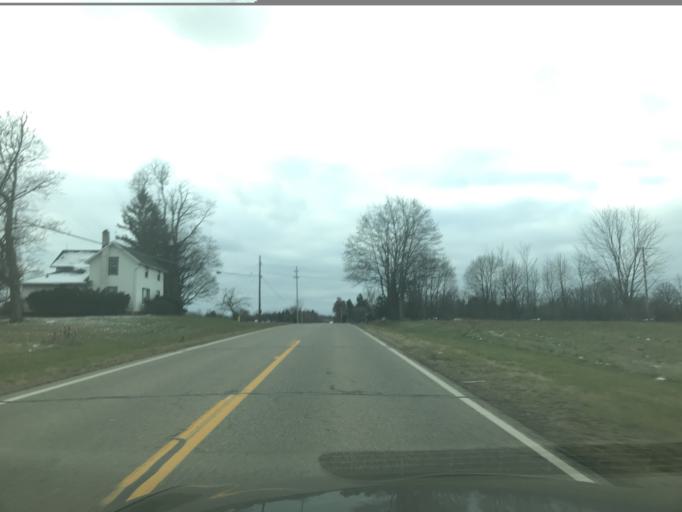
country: US
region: Michigan
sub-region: Eaton County
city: Waverly
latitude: 42.7328
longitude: -84.6817
